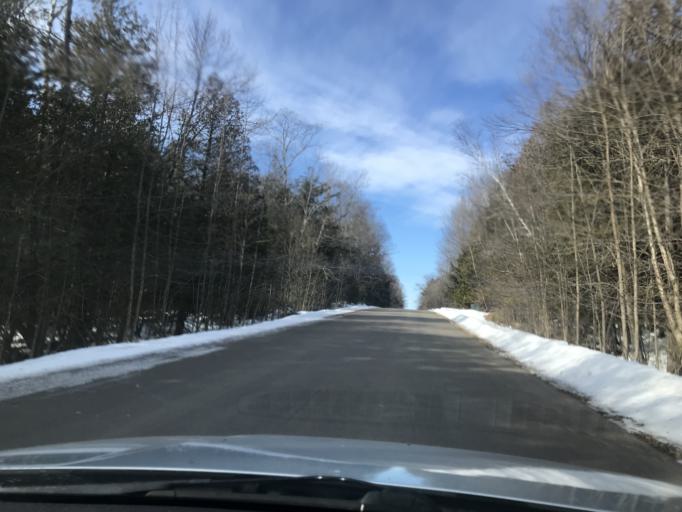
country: US
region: Wisconsin
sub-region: Oconto County
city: Gillett
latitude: 44.9616
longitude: -88.2765
